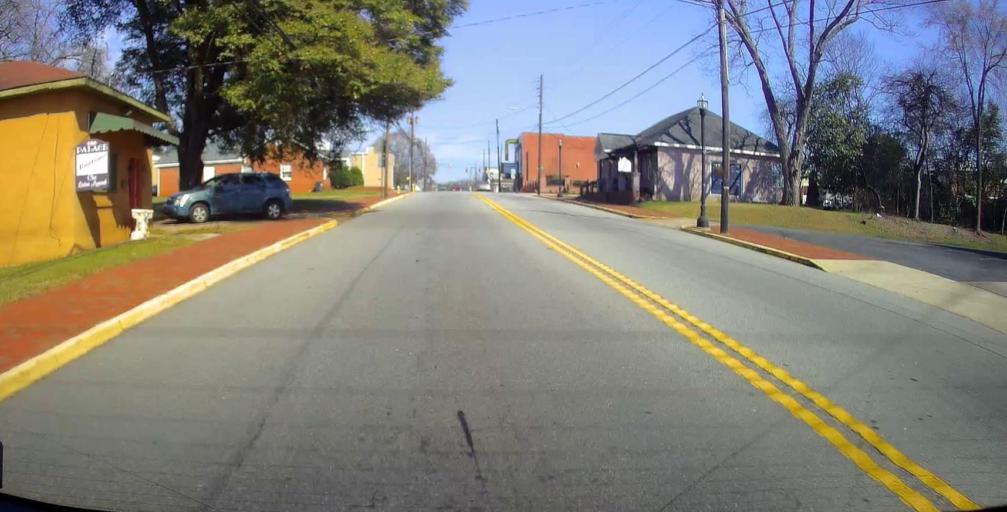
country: US
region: Georgia
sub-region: Houston County
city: Perry
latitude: 32.4585
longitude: -83.7354
